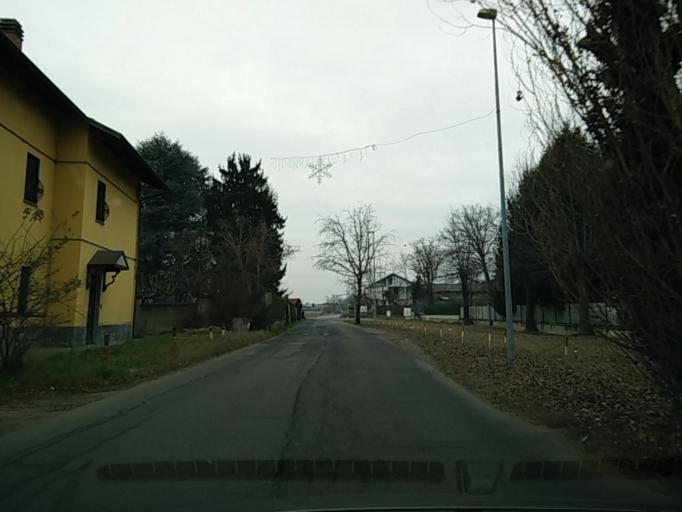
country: IT
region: Piedmont
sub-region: Provincia di Torino
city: Leini
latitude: 45.1516
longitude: 7.7182
